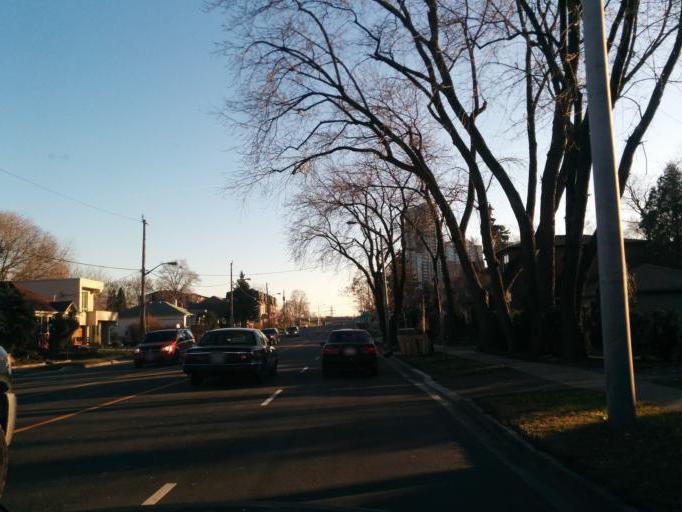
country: CA
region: Ontario
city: Etobicoke
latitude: 43.6444
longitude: -79.5365
